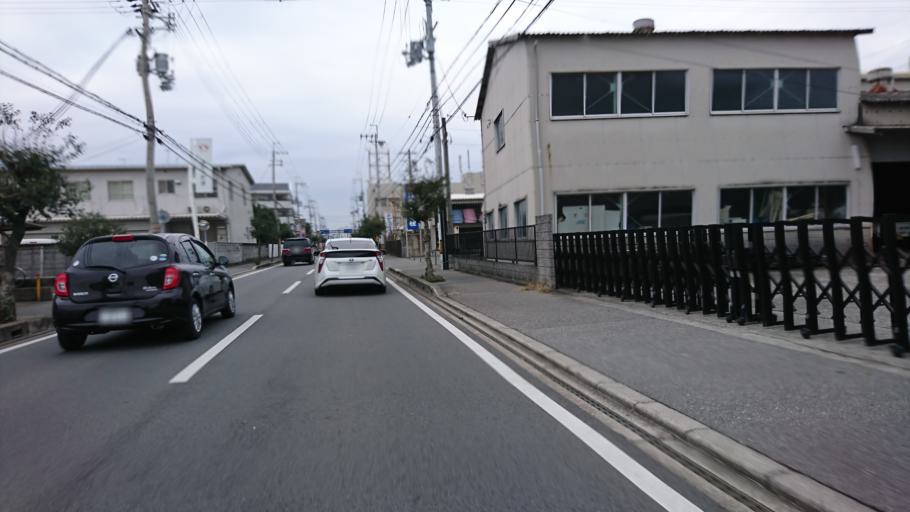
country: JP
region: Hyogo
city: Kakogawacho-honmachi
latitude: 34.7671
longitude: 134.8262
